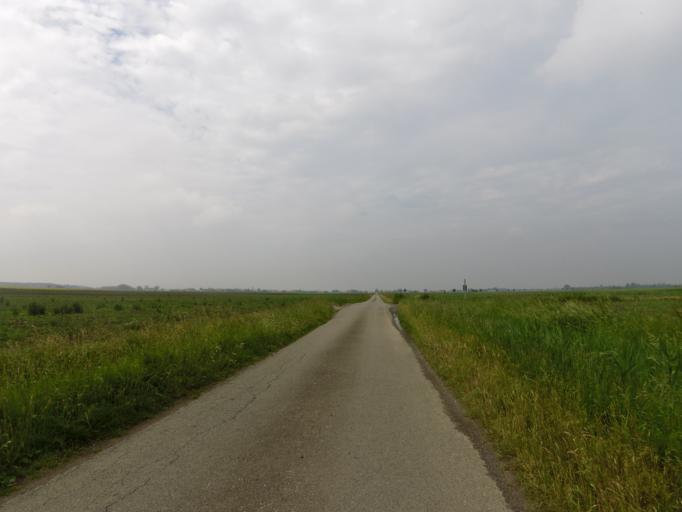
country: BE
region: Flanders
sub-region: Provincie West-Vlaanderen
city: Gistel
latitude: 51.1247
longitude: 2.9371
